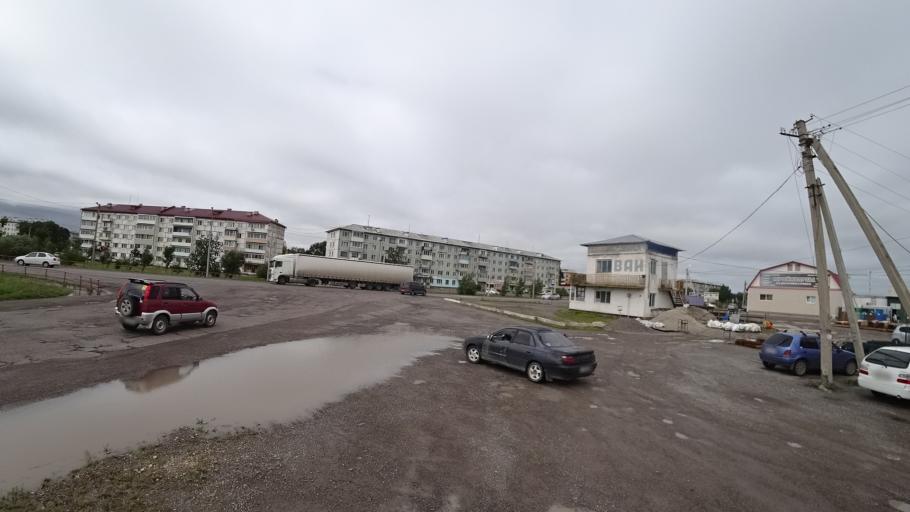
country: RU
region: Primorskiy
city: Monastyrishche
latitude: 44.2041
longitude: 132.4509
